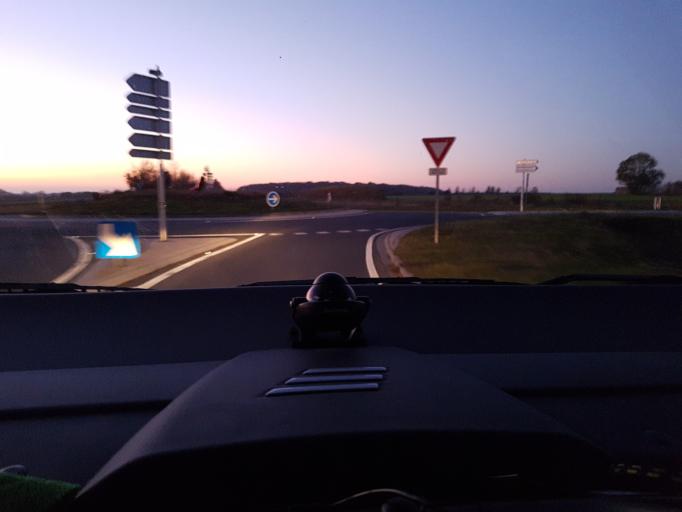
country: FR
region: Picardie
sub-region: Departement de la Somme
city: Saint-Valery-sur-Somme
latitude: 50.1763
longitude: 1.6138
